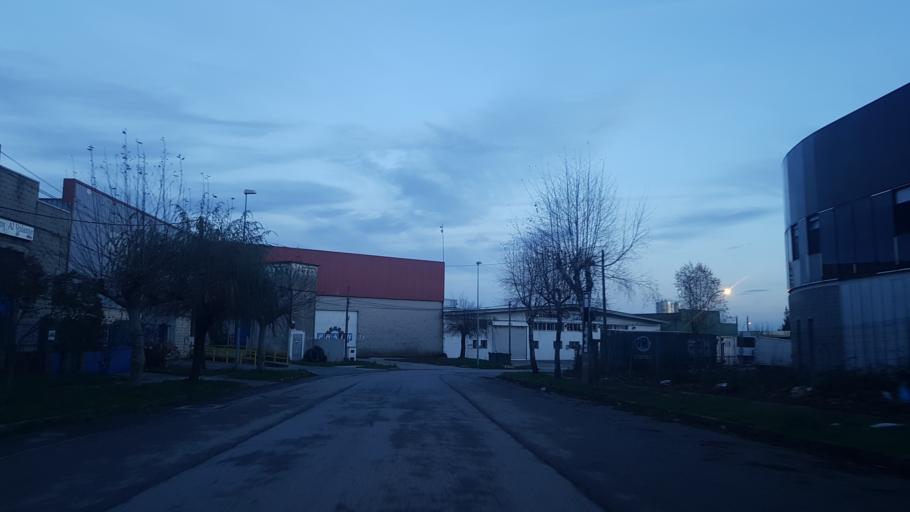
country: ES
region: Galicia
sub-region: Provincia de Lugo
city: Lugo
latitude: 43.0464
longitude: -7.5738
